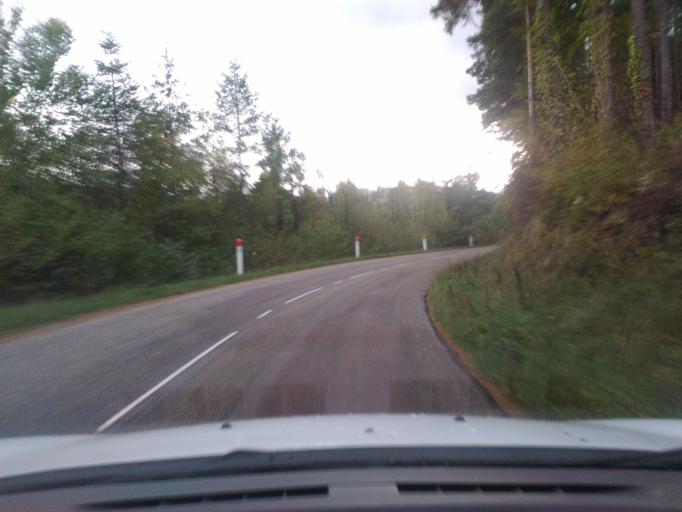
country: FR
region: Lorraine
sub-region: Departement des Vosges
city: Saint-Die-des-Vosges
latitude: 48.3203
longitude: 6.9770
